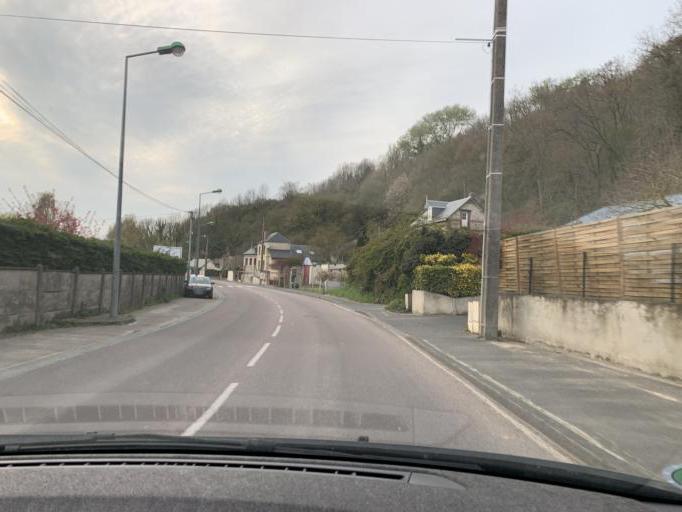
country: FR
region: Haute-Normandie
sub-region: Departement de la Seine-Maritime
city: Fecamp
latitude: 49.7535
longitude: 0.4072
